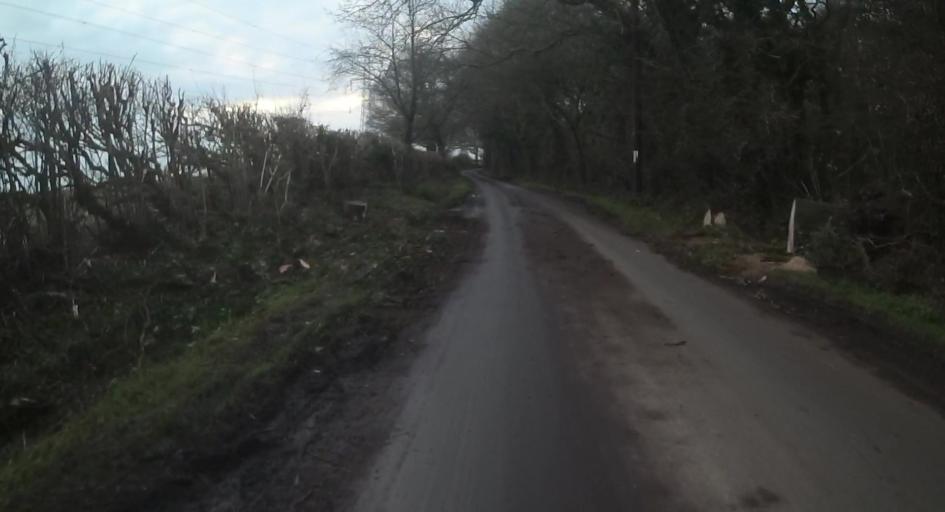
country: GB
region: England
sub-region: Hampshire
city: Kingsclere
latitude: 51.3005
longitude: -1.2348
